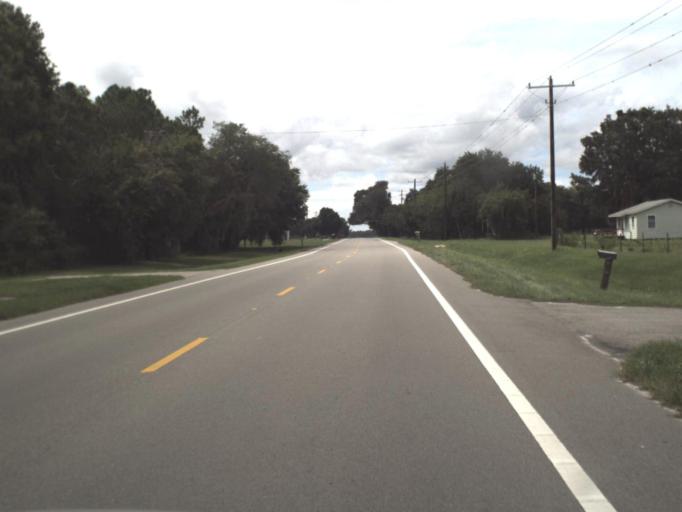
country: US
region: Florida
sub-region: Hillsborough County
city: Sun City Center
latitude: 27.5944
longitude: -82.3542
